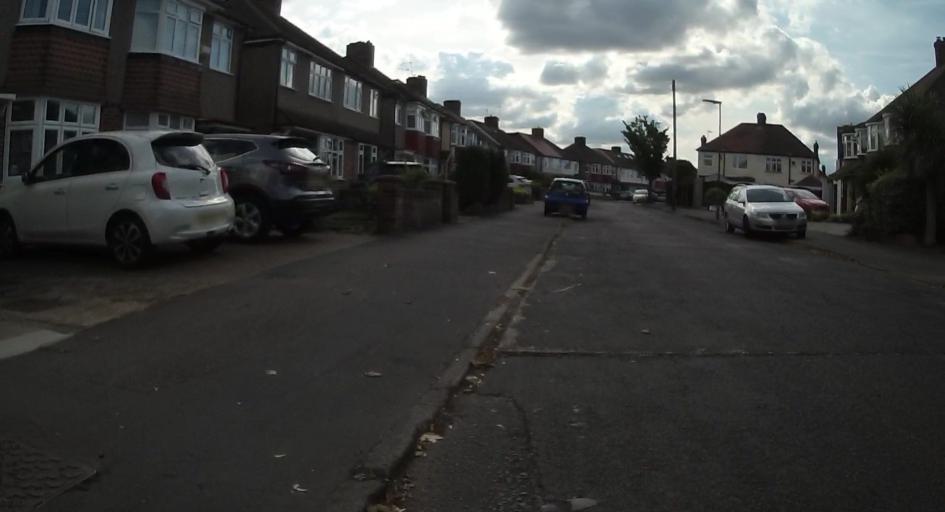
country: GB
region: England
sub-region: Surrey
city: Walton-on-Thames
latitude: 51.3847
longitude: -0.4058
